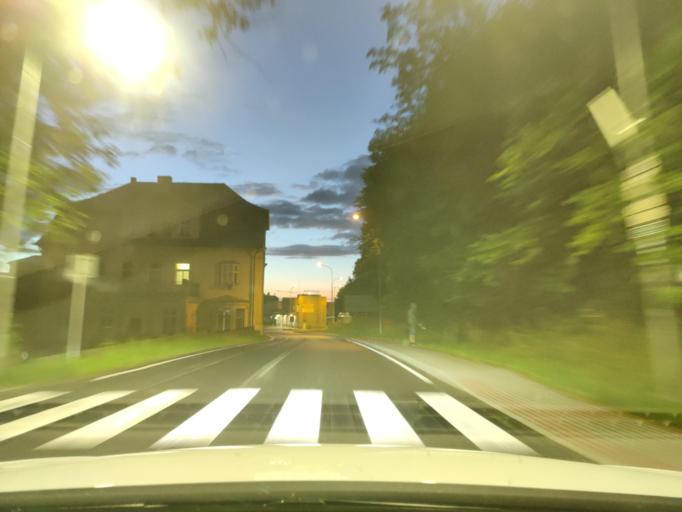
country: CZ
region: Olomoucky
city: Zlate Hory
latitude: 50.2598
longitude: 17.3984
